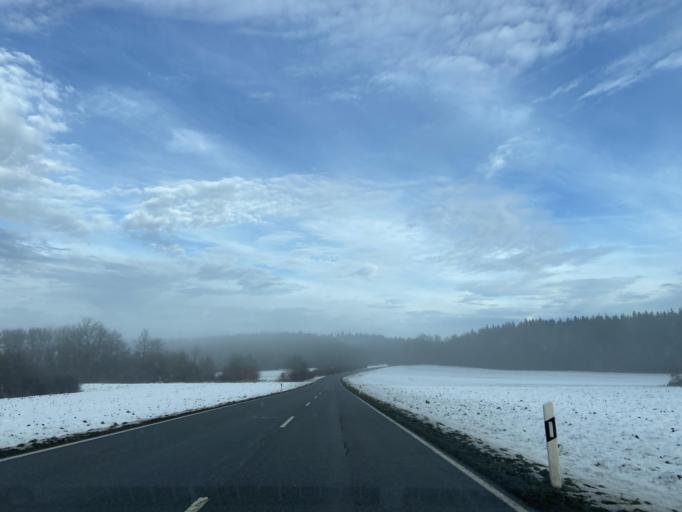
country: DE
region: Baden-Wuerttemberg
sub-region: Tuebingen Region
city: Hettingen
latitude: 48.2180
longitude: 9.2851
